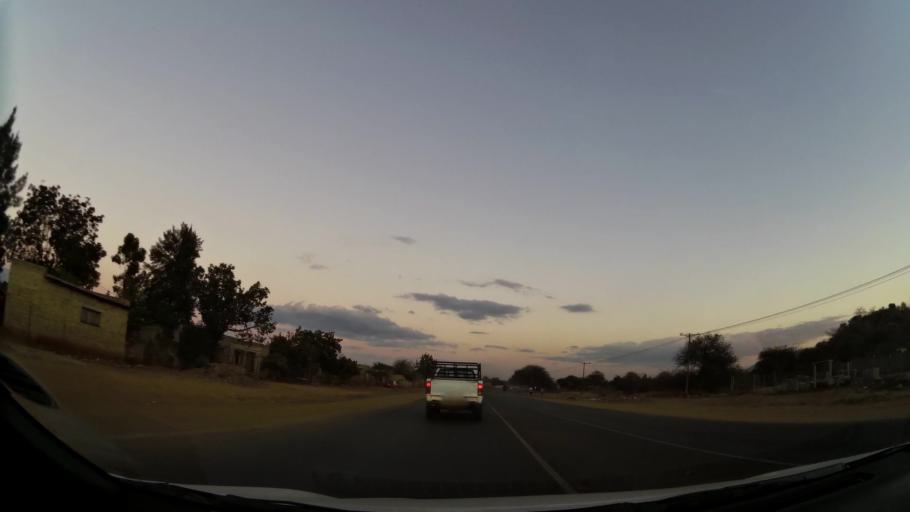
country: ZA
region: Limpopo
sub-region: Waterberg District Municipality
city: Mokopane
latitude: -24.1645
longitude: 28.9836
